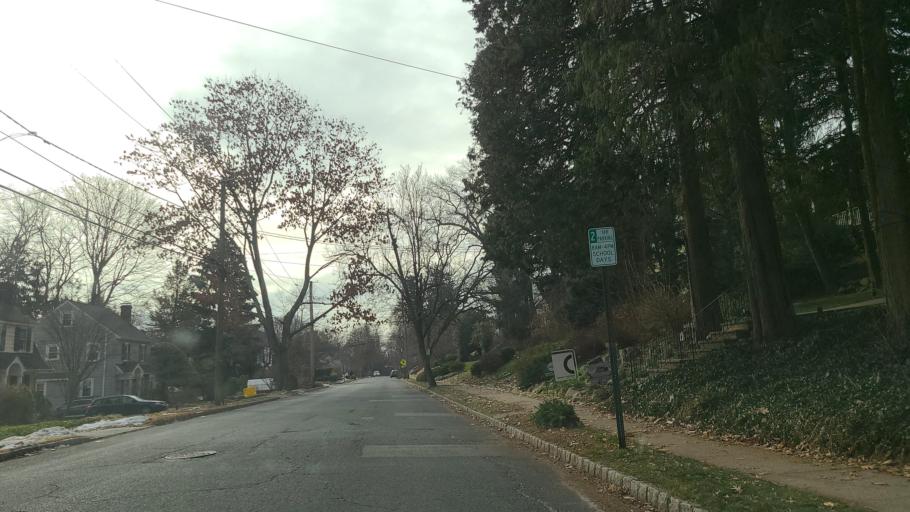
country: US
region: New Jersey
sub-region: Essex County
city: Maplewood
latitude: 40.7382
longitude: -74.2702
